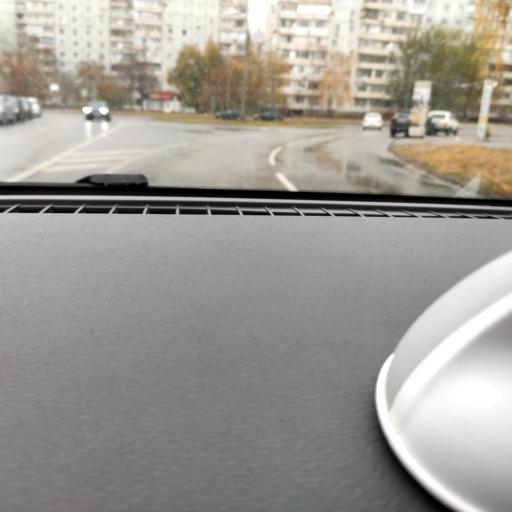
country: RU
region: Samara
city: Samara
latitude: 53.2606
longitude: 50.2297
